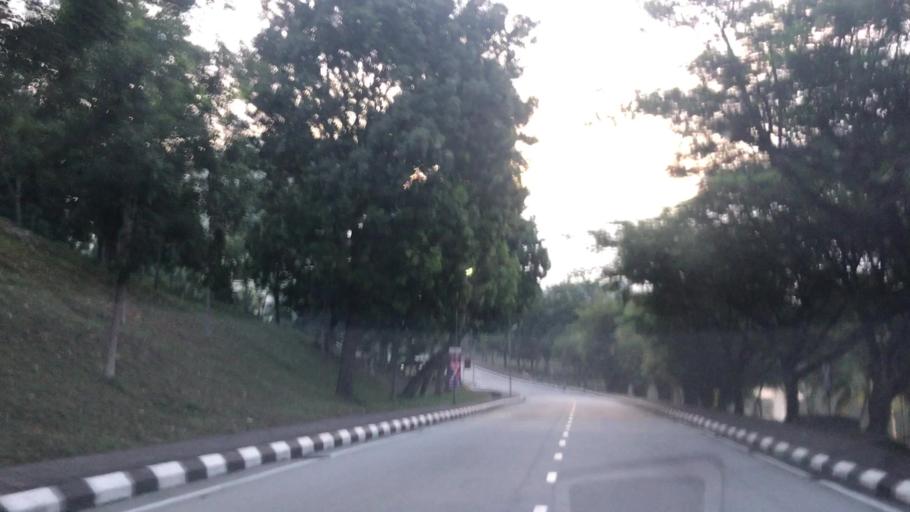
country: MY
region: Kuala Lumpur
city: Kuala Lumpur
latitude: 3.1186
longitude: 101.6579
